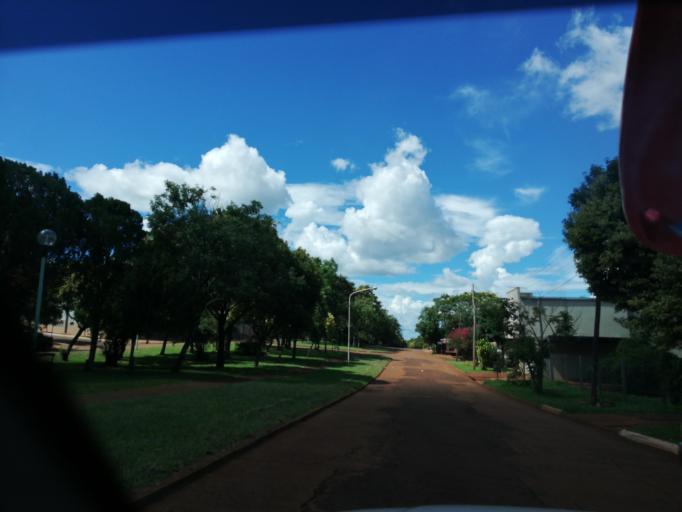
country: AR
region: Misiones
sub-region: Departamento de Apostoles
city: Apostoles
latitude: -27.9146
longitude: -55.7480
